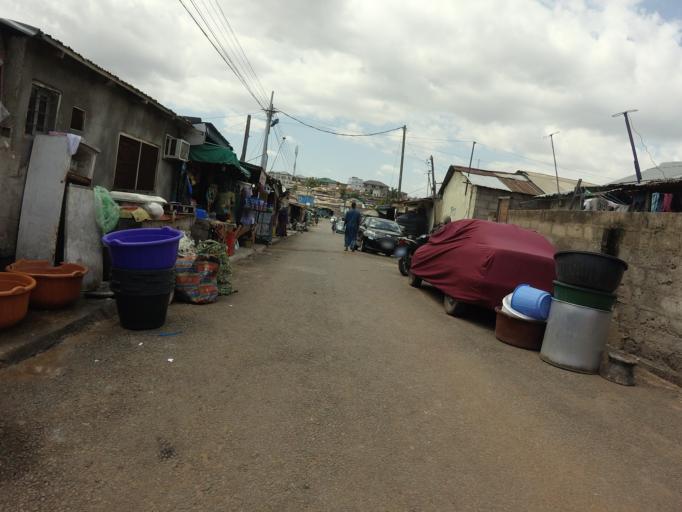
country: GH
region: Greater Accra
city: Accra
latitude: 5.5845
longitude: -0.2011
